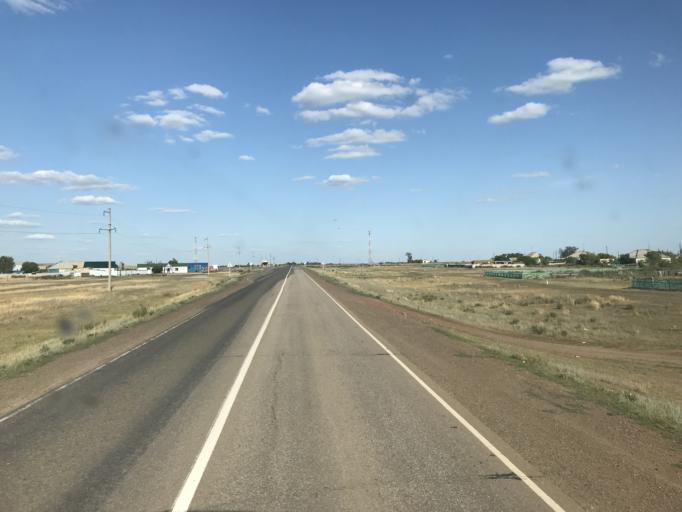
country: KZ
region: Aqmola
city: Esil
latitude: 51.8966
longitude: 66.7544
